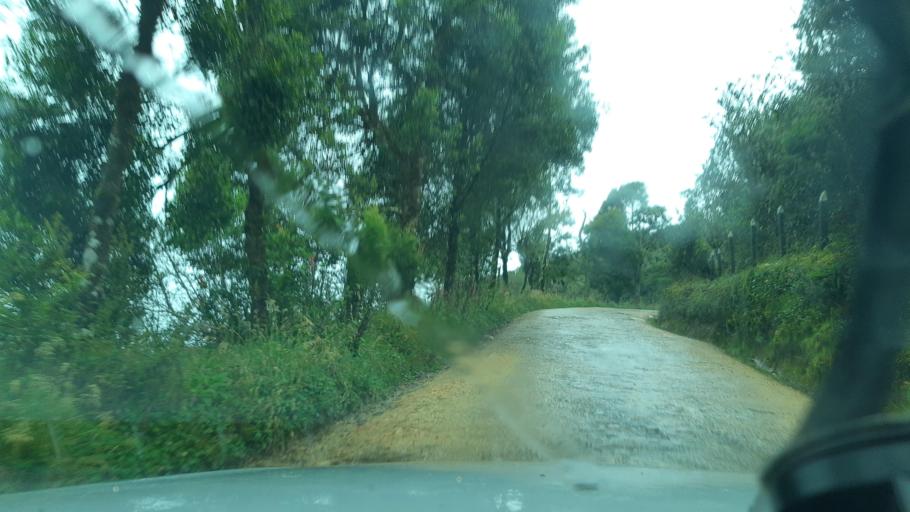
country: CO
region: Cundinamarca
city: Umbita
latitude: 5.2175
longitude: -73.5218
